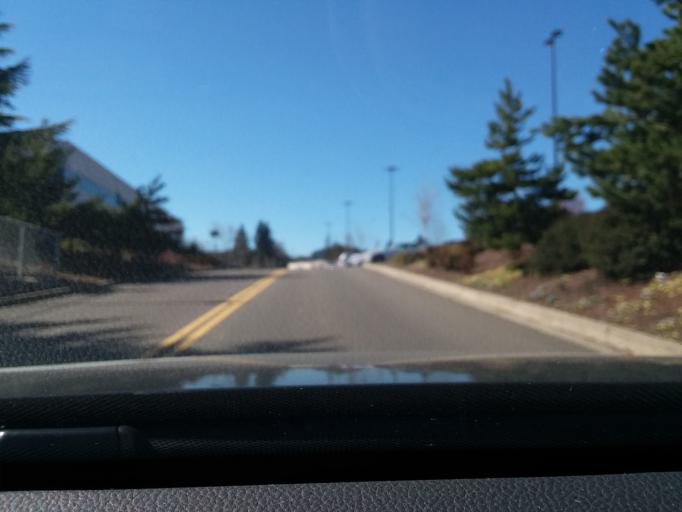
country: US
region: Washington
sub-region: Pierce County
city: Tacoma
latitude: 47.2390
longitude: -122.4783
